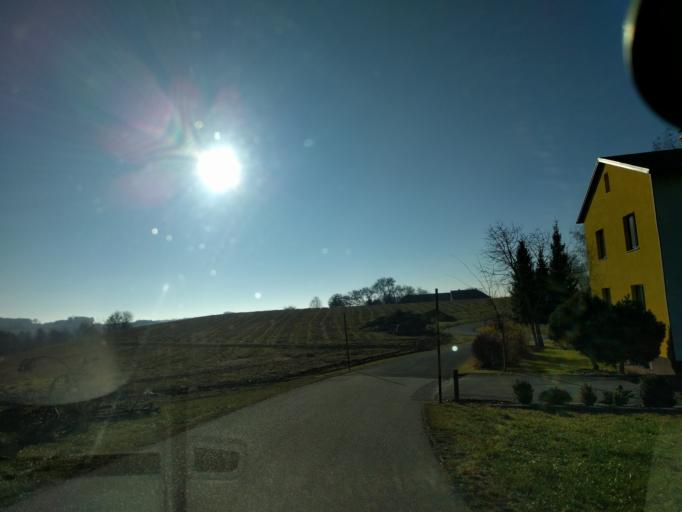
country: AT
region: Upper Austria
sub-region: Politischer Bezirk Urfahr-Umgebung
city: Kirchschlag bei Linz
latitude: 48.3949
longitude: 14.2901
